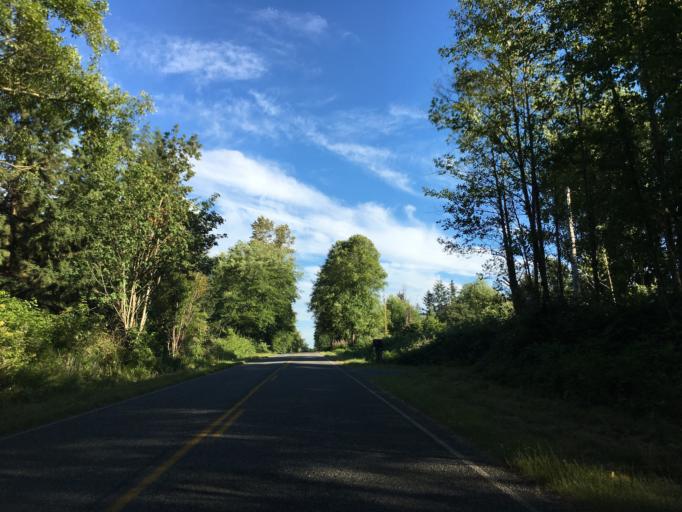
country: US
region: Washington
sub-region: Whatcom County
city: Sudden Valley
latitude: 48.6572
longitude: -122.3701
